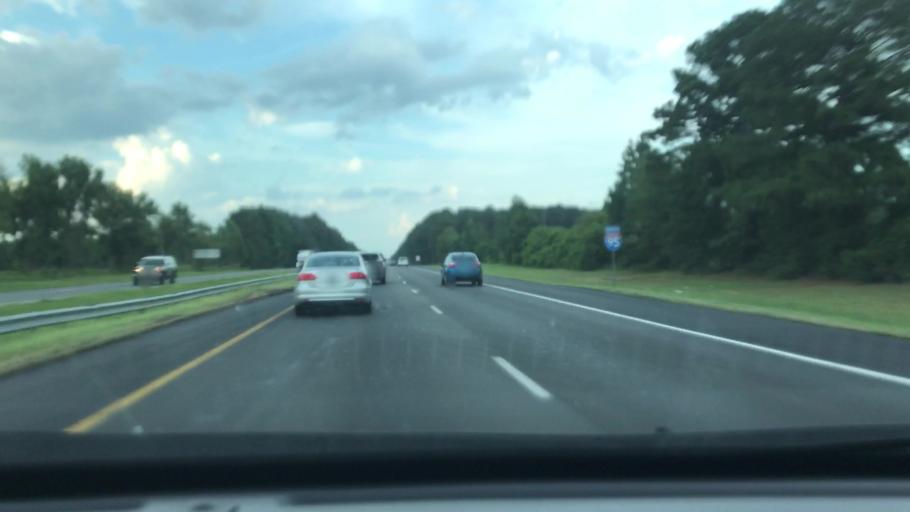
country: US
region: North Carolina
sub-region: Cumberland County
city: Eastover
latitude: 35.1352
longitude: -78.7414
